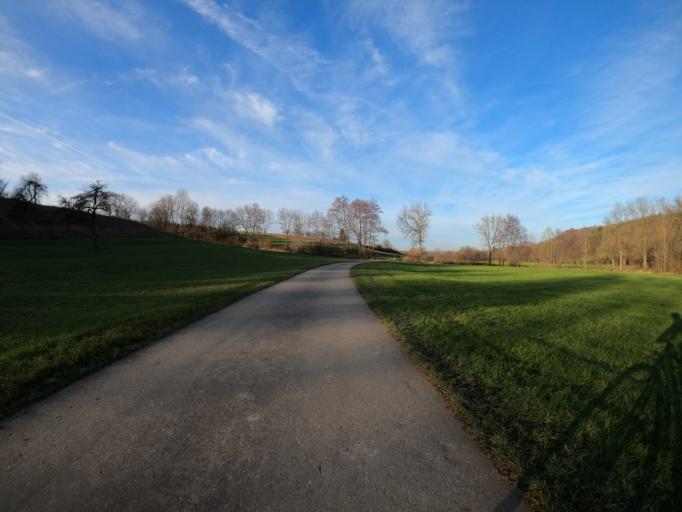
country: DE
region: Baden-Wuerttemberg
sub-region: Regierungsbezirk Stuttgart
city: Hattenhofen
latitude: 48.6574
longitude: 9.5802
